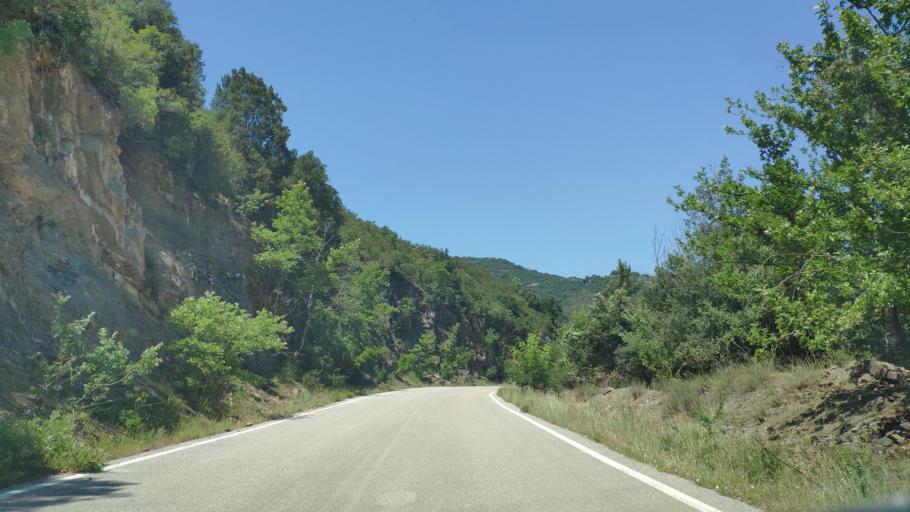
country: GR
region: West Greece
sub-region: Nomos Aitolias kai Akarnanias
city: Sardinia
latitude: 38.9223
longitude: 21.3643
